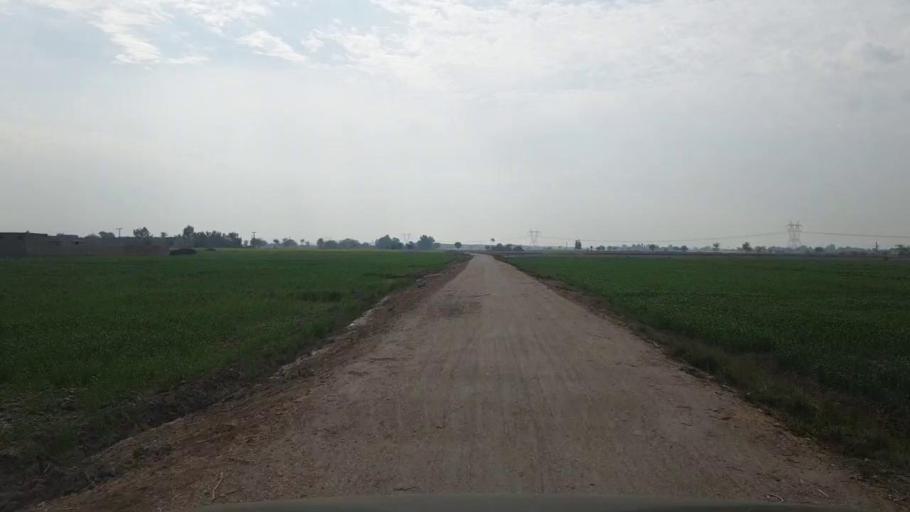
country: PK
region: Sindh
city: Hala
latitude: 25.9900
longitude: 68.4107
